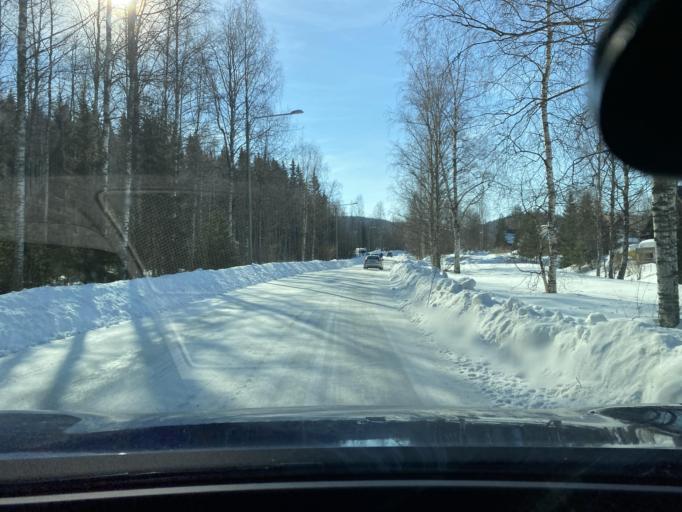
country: FI
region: Central Finland
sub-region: Jyvaeskylae
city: Muurame
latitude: 62.0944
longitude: 25.6438
